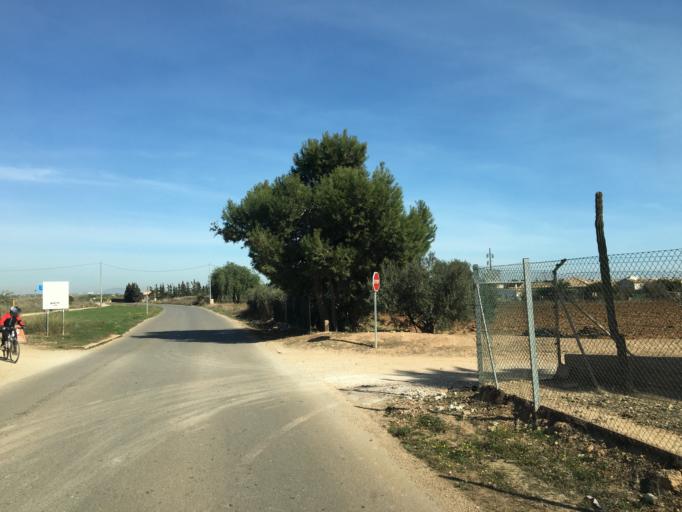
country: ES
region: Murcia
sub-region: Murcia
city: Cartagena
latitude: 37.6542
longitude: -1.0239
